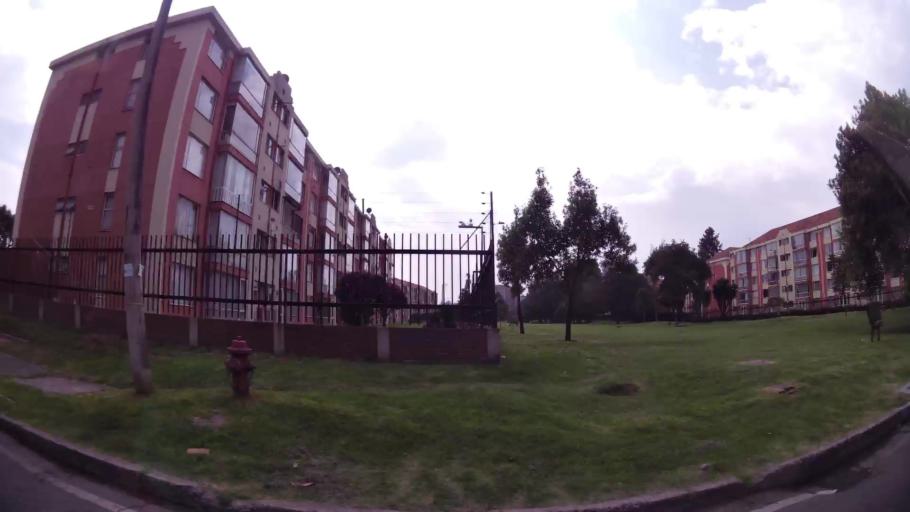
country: CO
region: Bogota D.C.
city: Barrio San Luis
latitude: 4.7312
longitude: -74.0576
